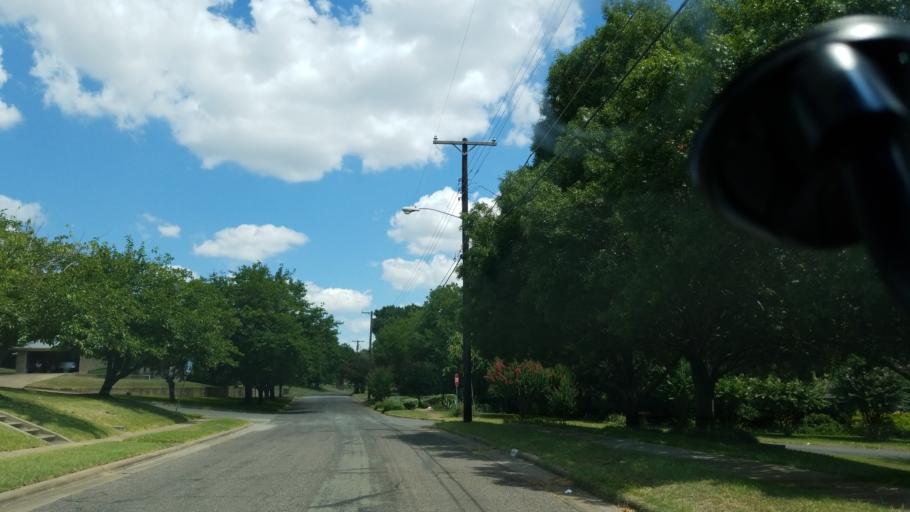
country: US
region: Texas
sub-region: Dallas County
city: Cockrell Hill
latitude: 32.7033
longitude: -96.8446
